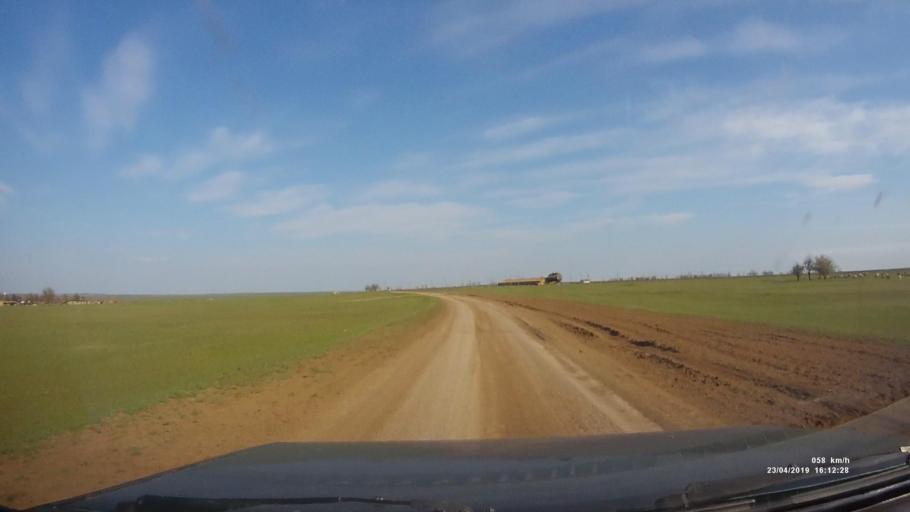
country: RU
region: Kalmykiya
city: Priyutnoye
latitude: 46.4662
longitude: 43.1266
